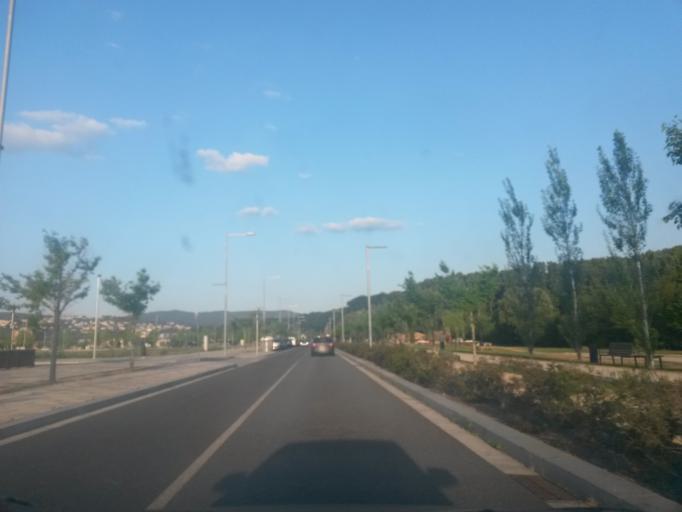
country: ES
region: Catalonia
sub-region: Provincia de Girona
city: Salt
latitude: 41.9899
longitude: 2.8003
